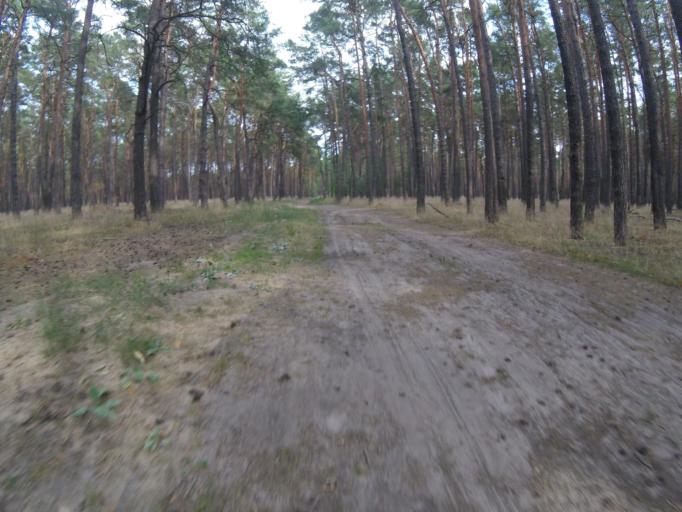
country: DE
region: Brandenburg
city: Wildau
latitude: 52.3179
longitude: 13.7320
